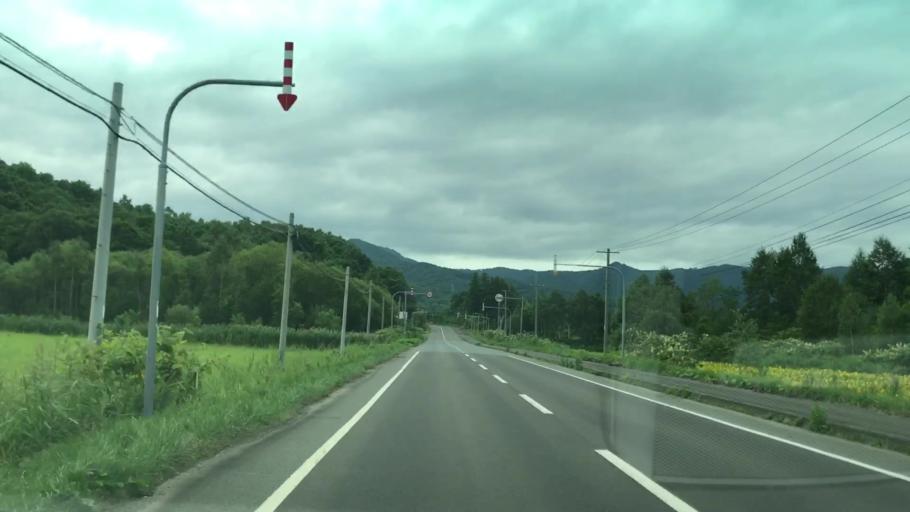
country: JP
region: Hokkaido
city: Yoichi
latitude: 43.0564
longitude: 140.8207
